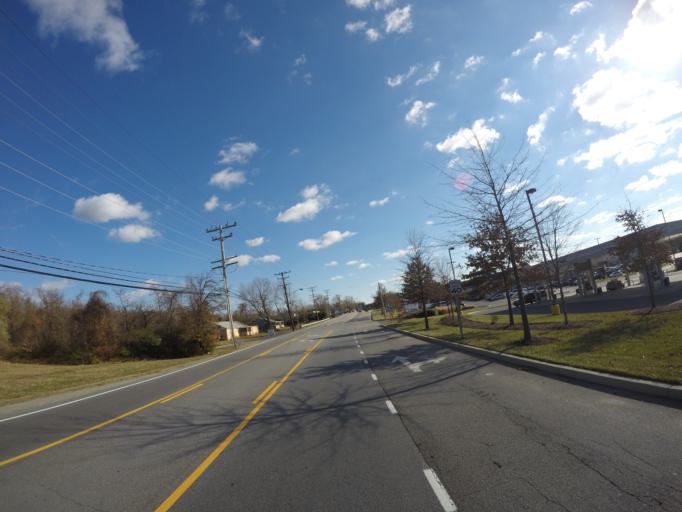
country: US
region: Maryland
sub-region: Anne Arundel County
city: Lake Shore
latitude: 39.1213
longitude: -76.5124
